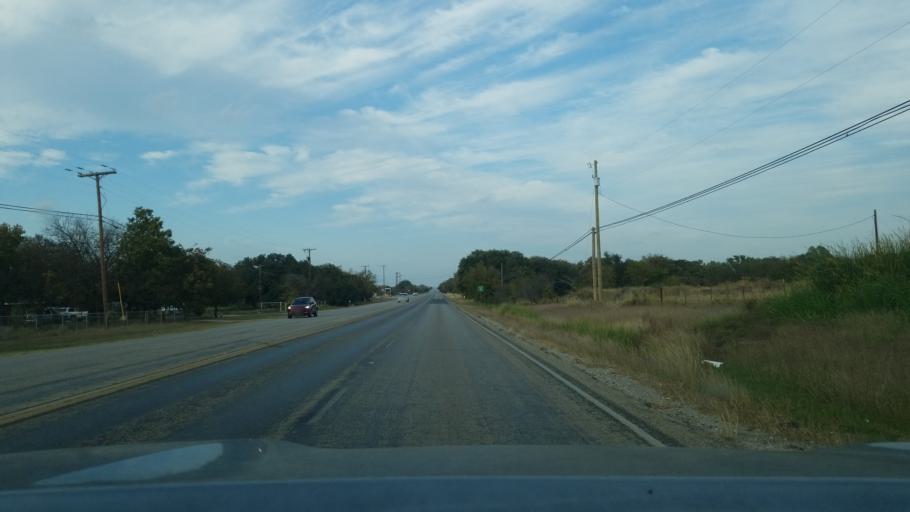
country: US
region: Texas
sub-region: Brown County
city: Early
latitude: 31.7541
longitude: -98.9608
